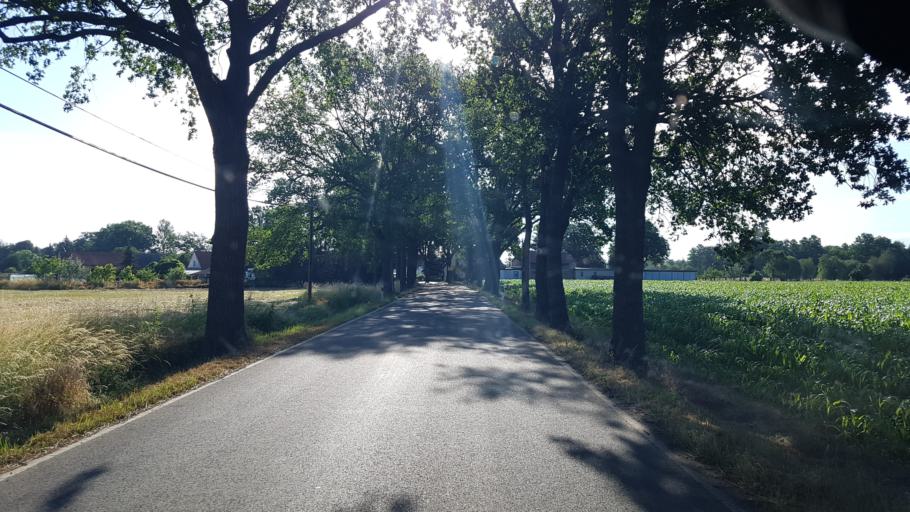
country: DE
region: Brandenburg
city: Kasel-Golzig
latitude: 51.9568
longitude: 13.6650
